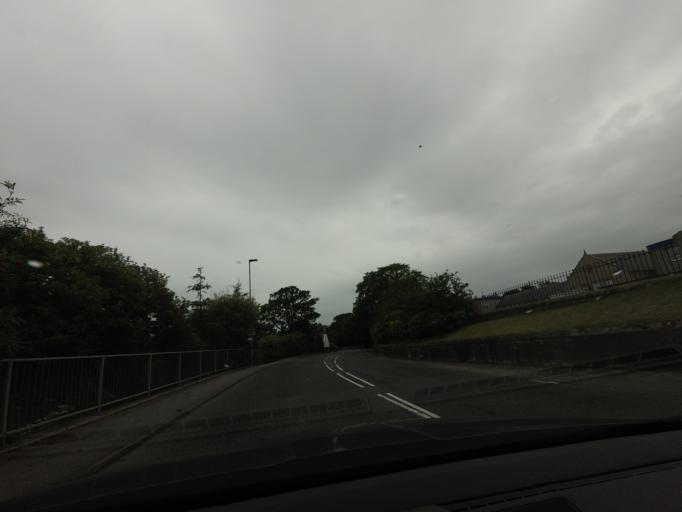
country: GB
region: Scotland
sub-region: Aberdeenshire
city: Portsoy
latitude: 57.6796
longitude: -2.6873
